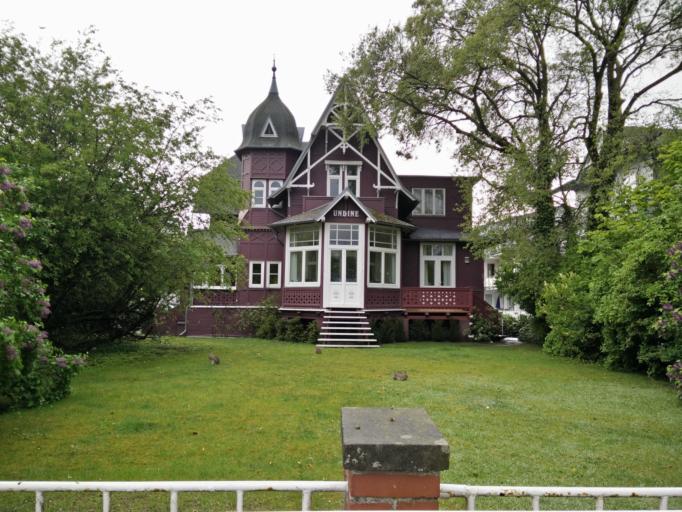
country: DE
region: Mecklenburg-Vorpommern
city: Ostseebad Binz
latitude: 54.4034
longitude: 13.6121
